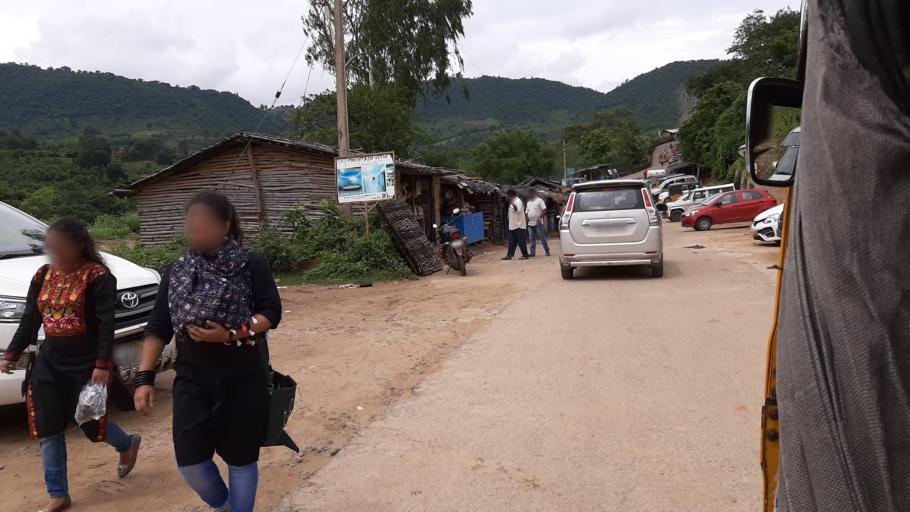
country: IN
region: Andhra Pradesh
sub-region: Vizianagaram District
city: Salur
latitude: 18.2785
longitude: 83.0377
